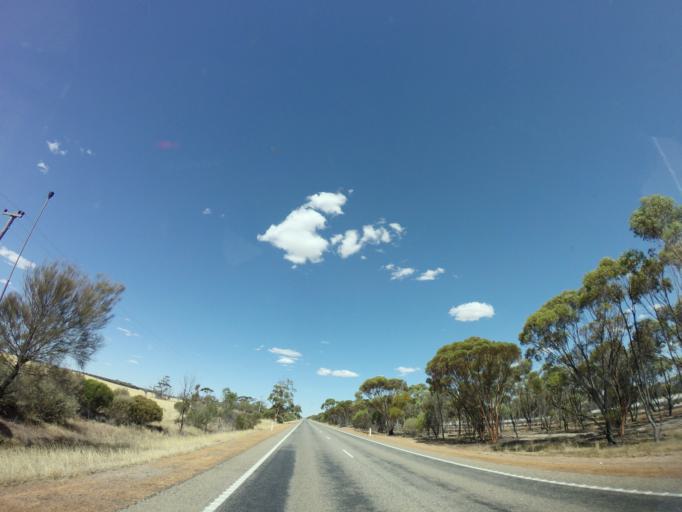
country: AU
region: Western Australia
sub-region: Cunderdin
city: Cunderdin
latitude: -31.6245
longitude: 117.5802
